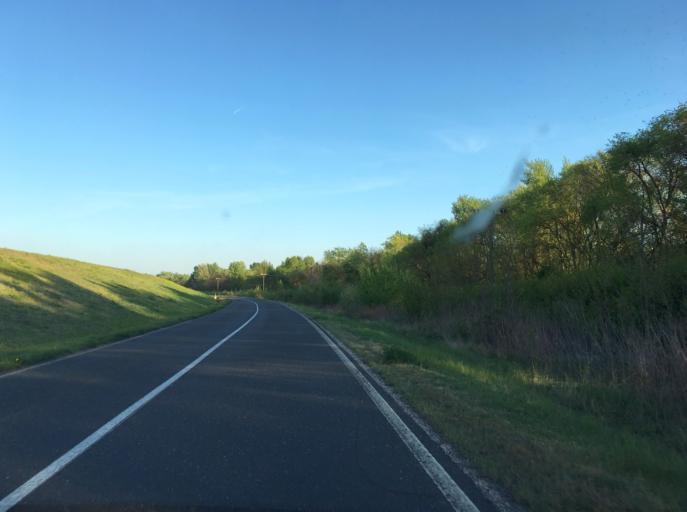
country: HU
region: Gyor-Moson-Sopron
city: Rajka
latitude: 48.0042
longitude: 17.2545
